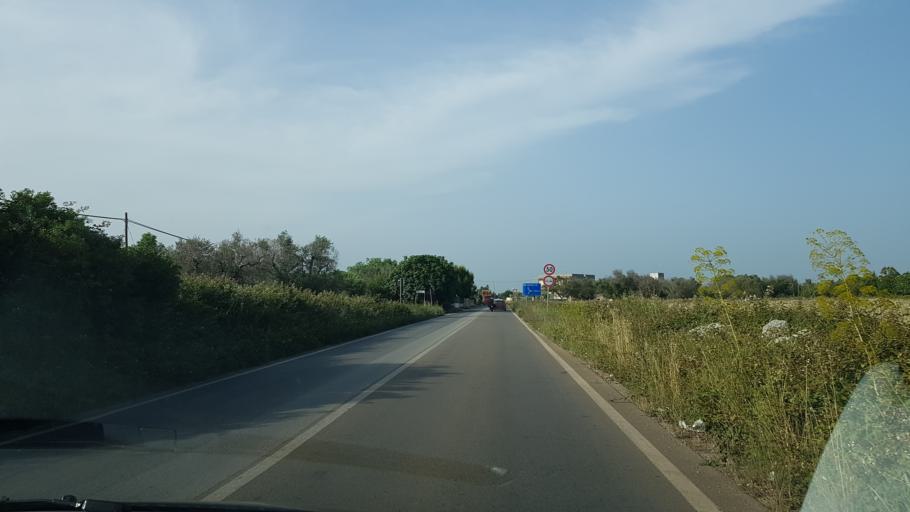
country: IT
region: Apulia
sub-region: Provincia di Lecce
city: Porto Cesareo
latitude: 40.3001
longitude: 17.8583
